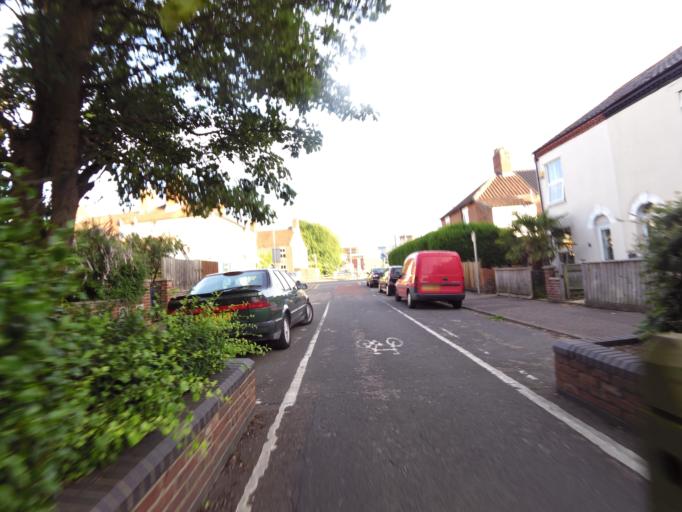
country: GB
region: England
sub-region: Norfolk
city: Norwich
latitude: 52.6393
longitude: 1.2943
